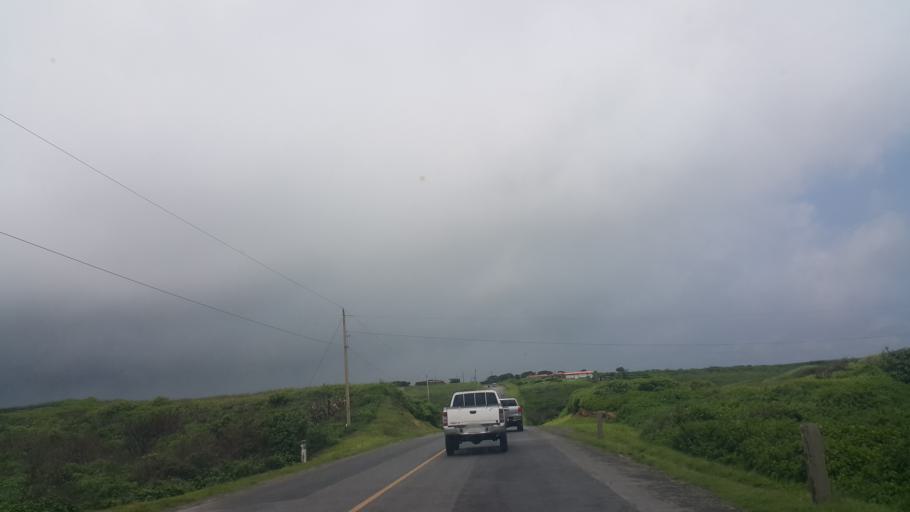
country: NI
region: Managua
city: El Crucero
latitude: 11.9433
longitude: -86.2982
